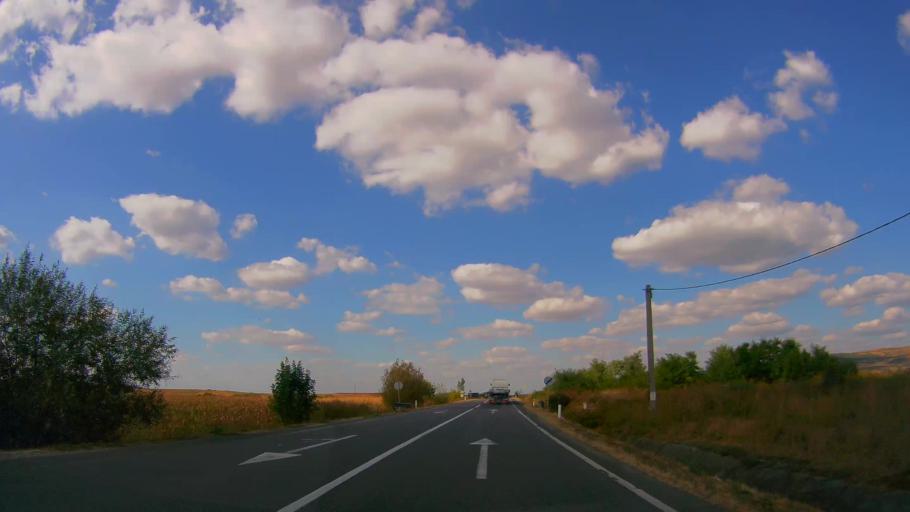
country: RO
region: Salaj
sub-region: Comuna Sarmasag
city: Sarmasag
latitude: 47.3507
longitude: 22.8007
